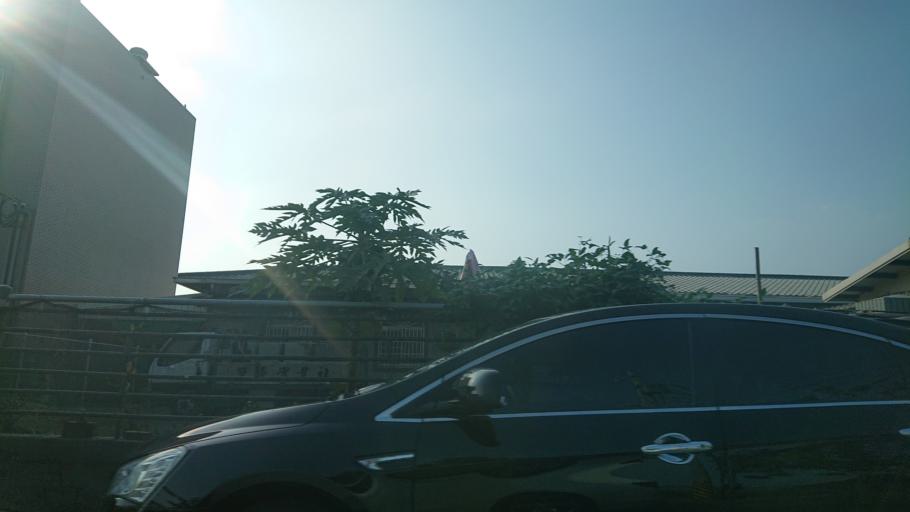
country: TW
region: Taiwan
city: Xinying
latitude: 23.1951
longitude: 120.2716
